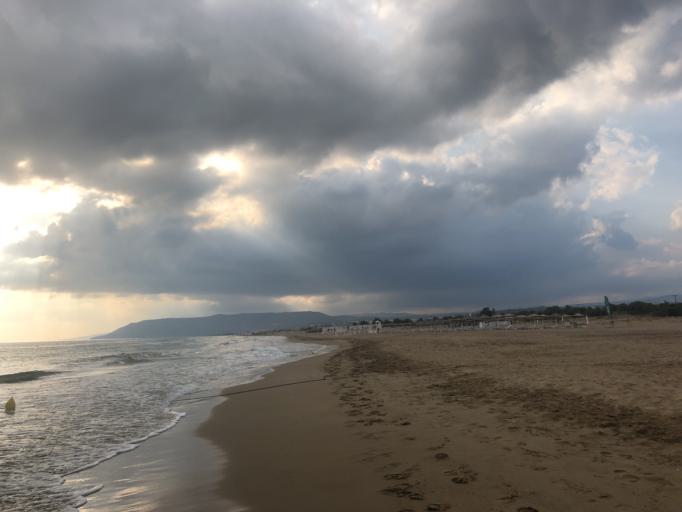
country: GR
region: Crete
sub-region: Nomos Chanias
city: Georgioupolis
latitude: 35.3564
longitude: 24.2802
